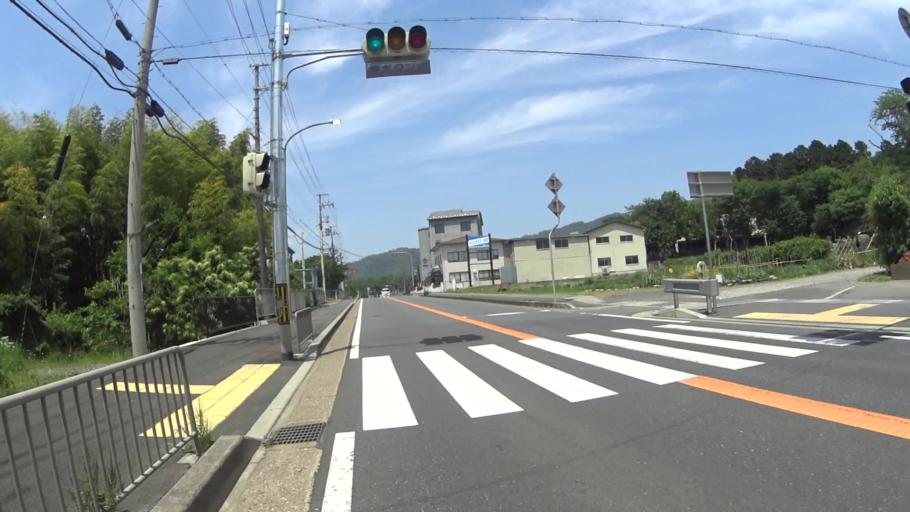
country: JP
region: Kyoto
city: Fukuchiyama
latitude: 35.2700
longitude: 135.1823
